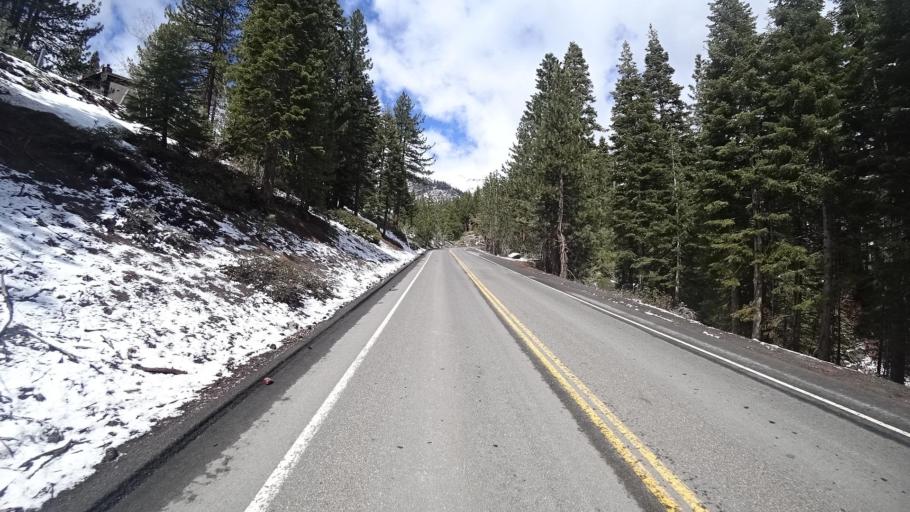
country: US
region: Nevada
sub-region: Washoe County
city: Incline Village
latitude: 39.2684
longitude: -119.9462
